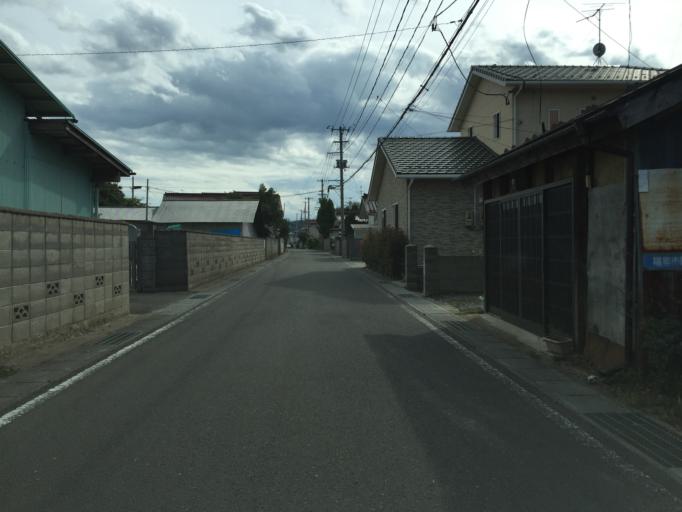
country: JP
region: Fukushima
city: Hobaramachi
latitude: 37.7932
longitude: 140.5118
